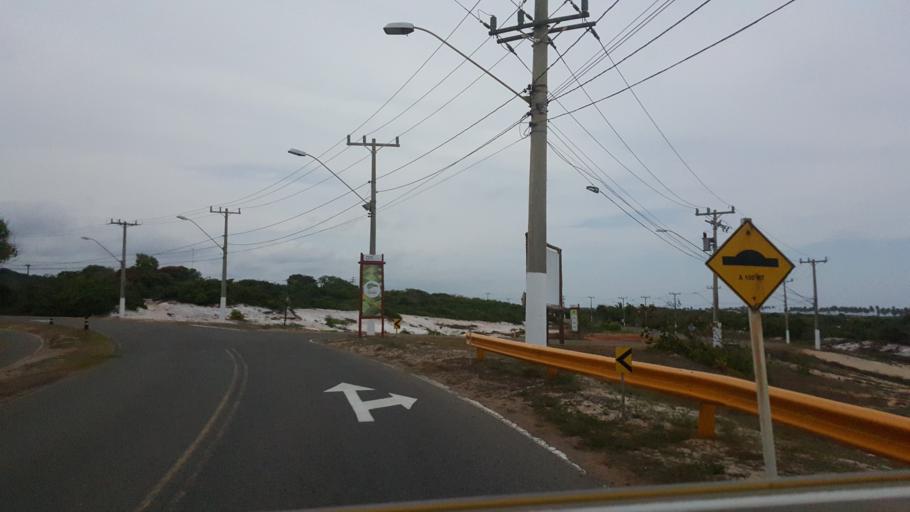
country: BR
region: Bahia
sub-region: Mata De Sao Joao
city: Mata de Sao Joao
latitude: -12.4308
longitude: -37.9188
